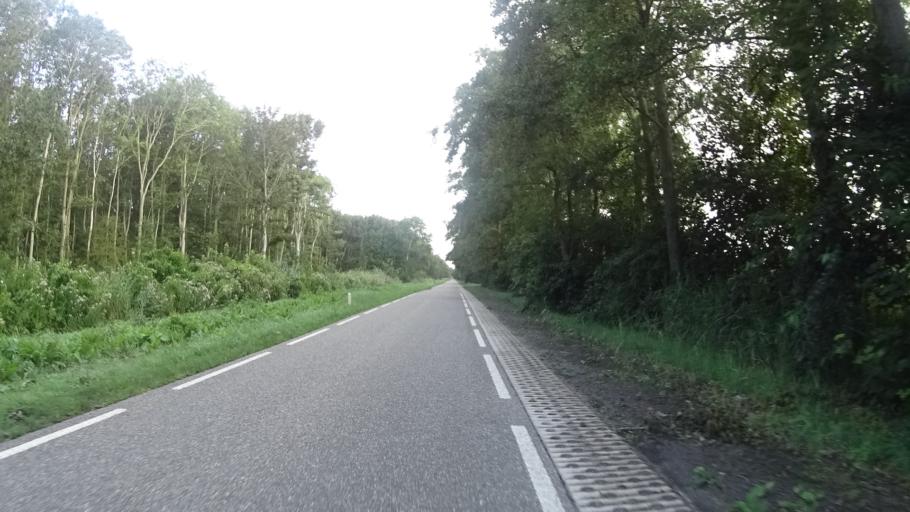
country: NL
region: North Holland
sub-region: Gemeente Hollands Kroon
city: Den Oever
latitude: 52.9124
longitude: 5.0569
